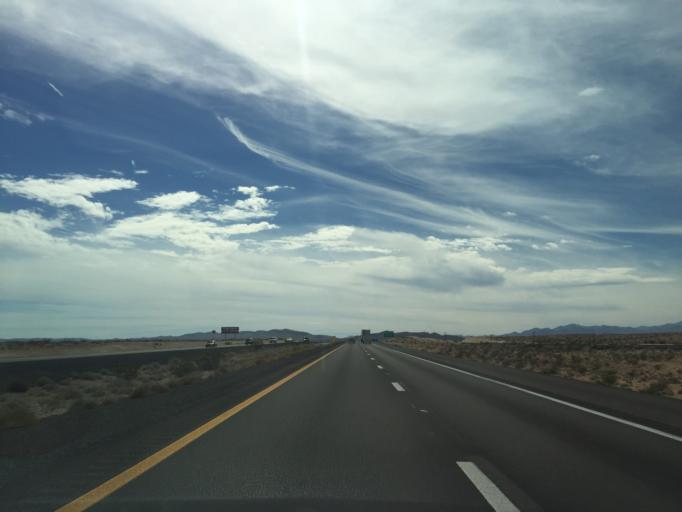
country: US
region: Nevada
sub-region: Clark County
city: Moapa Town
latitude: 36.5114
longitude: -114.7479
